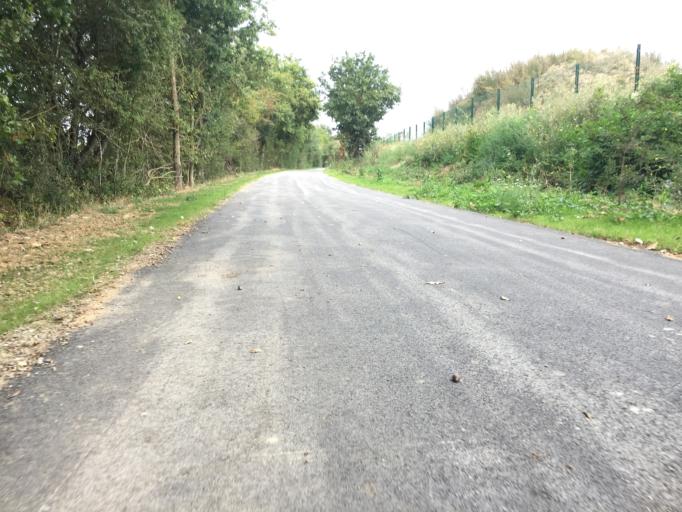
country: FR
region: Picardie
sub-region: Departement de l'Oise
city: Auneuil
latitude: 49.3819
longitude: 1.9936
